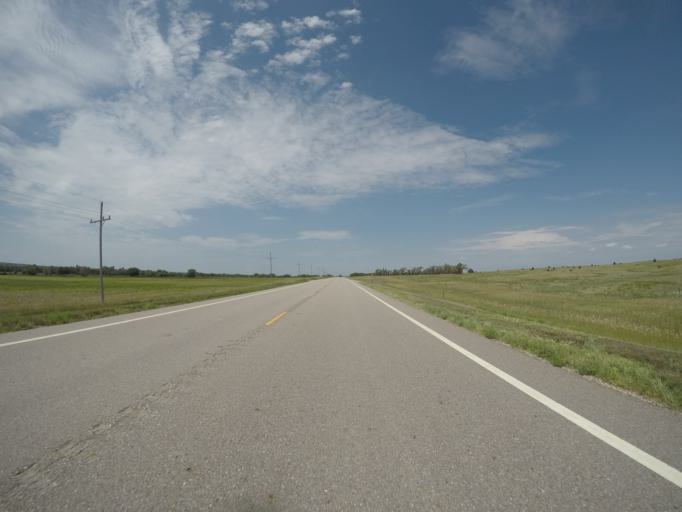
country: US
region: Kansas
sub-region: Rooks County
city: Stockton
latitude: 39.4444
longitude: -99.1797
